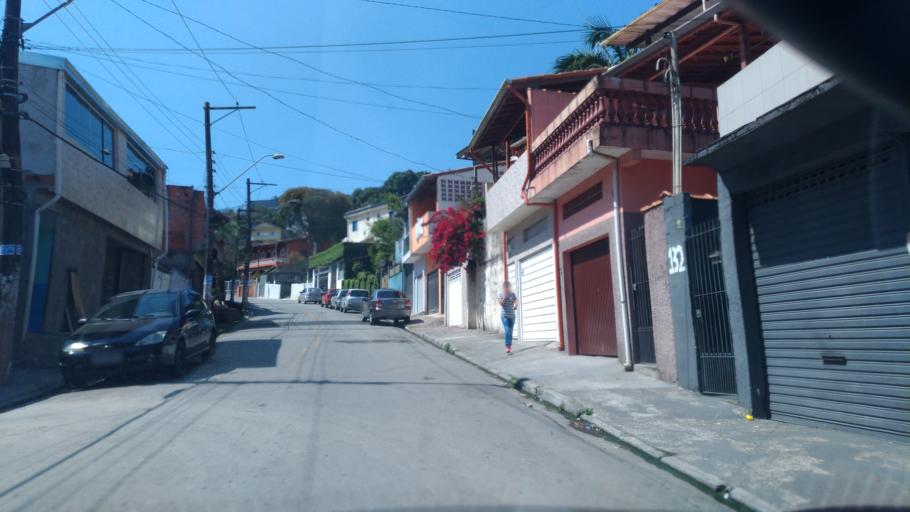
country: BR
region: Sao Paulo
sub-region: Sao Bernardo Do Campo
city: Sao Bernardo do Campo
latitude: -23.7757
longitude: -46.5200
